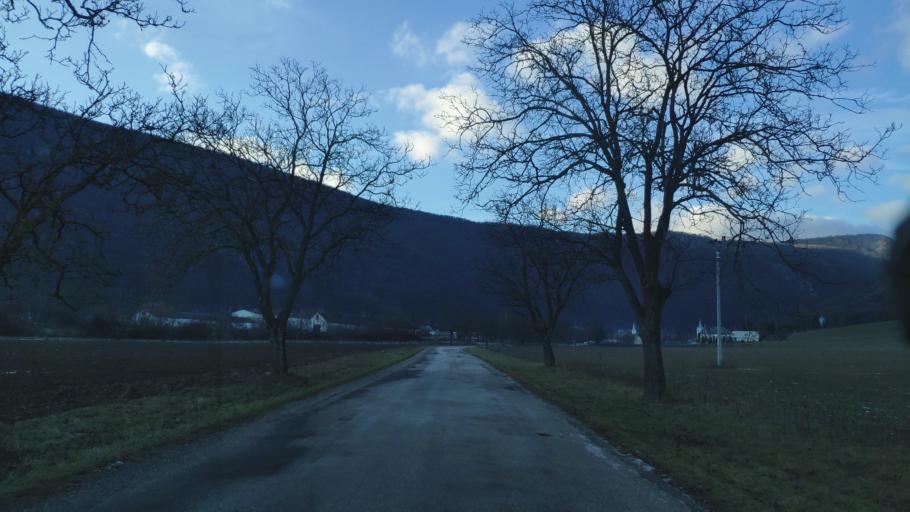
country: SK
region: Kosicky
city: Medzev
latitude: 48.6243
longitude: 20.8630
